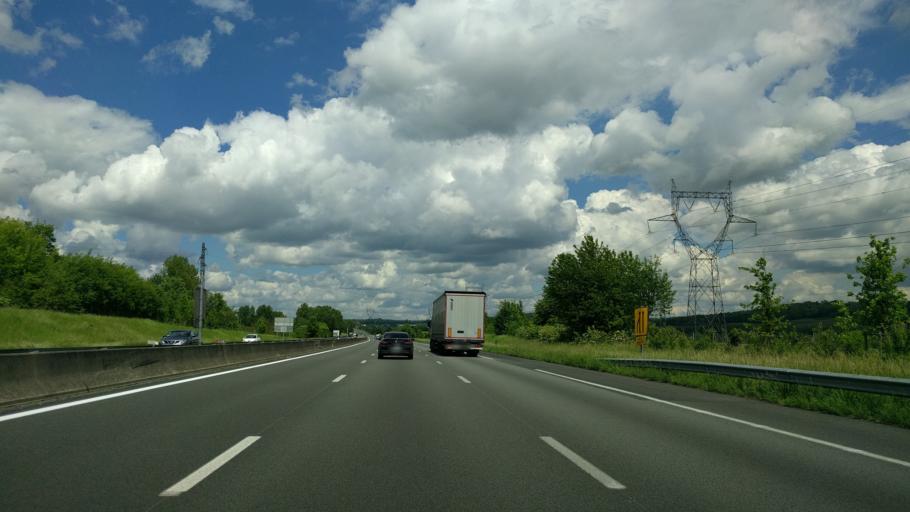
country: FR
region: Picardie
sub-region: Departement de l'Oise
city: Longueil-Sainte-Marie
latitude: 49.3642
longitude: 2.7040
